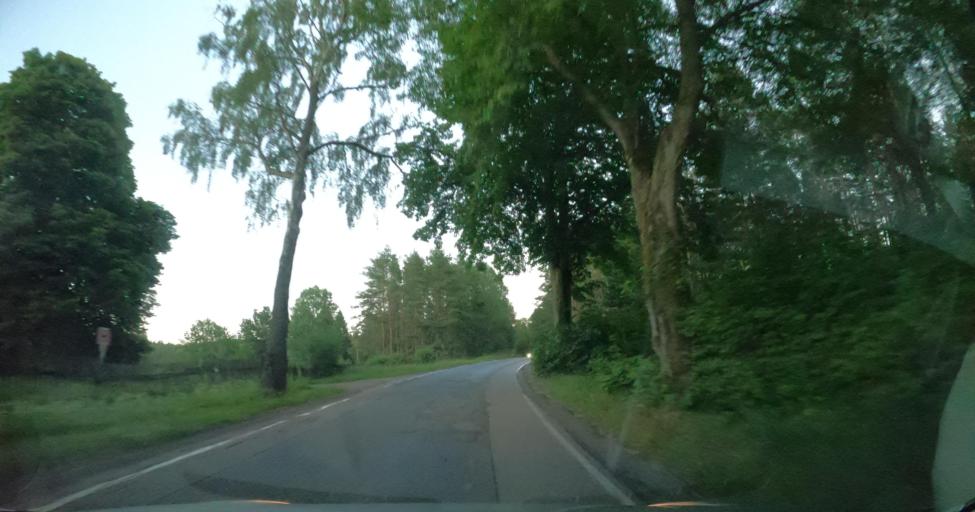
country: PL
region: Pomeranian Voivodeship
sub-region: Powiat wejherowski
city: Luzino
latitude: 54.4662
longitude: 18.1050
